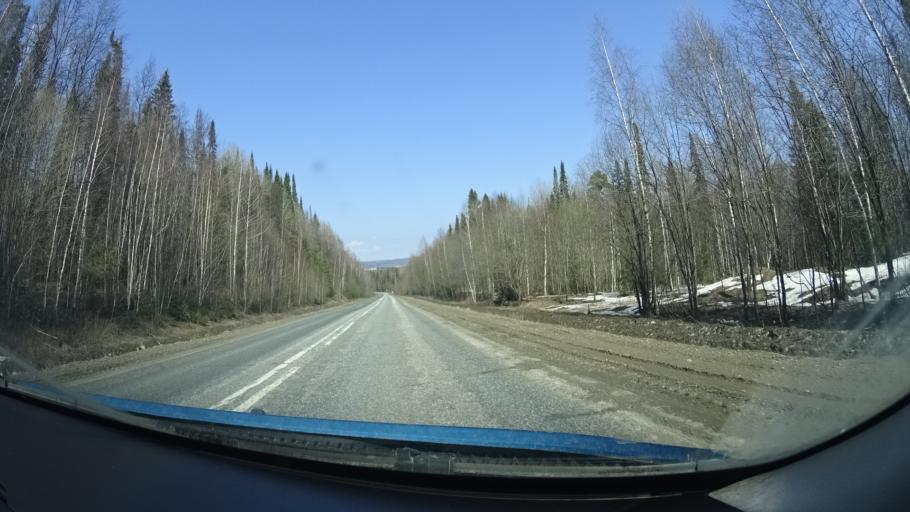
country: RU
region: Perm
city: Yugo-Kamskiy
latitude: 57.5105
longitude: 55.6853
